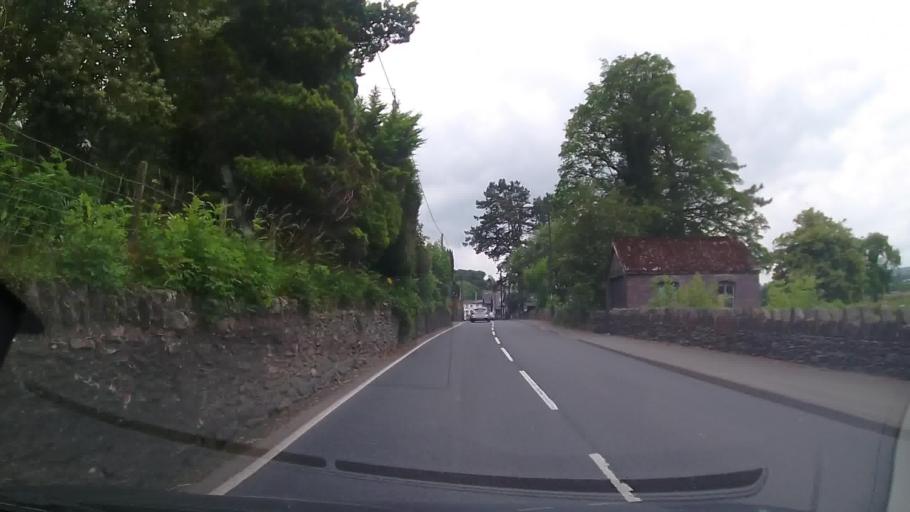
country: GB
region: Wales
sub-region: Denbighshire
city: Corwen
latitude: 52.9811
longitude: -3.3680
